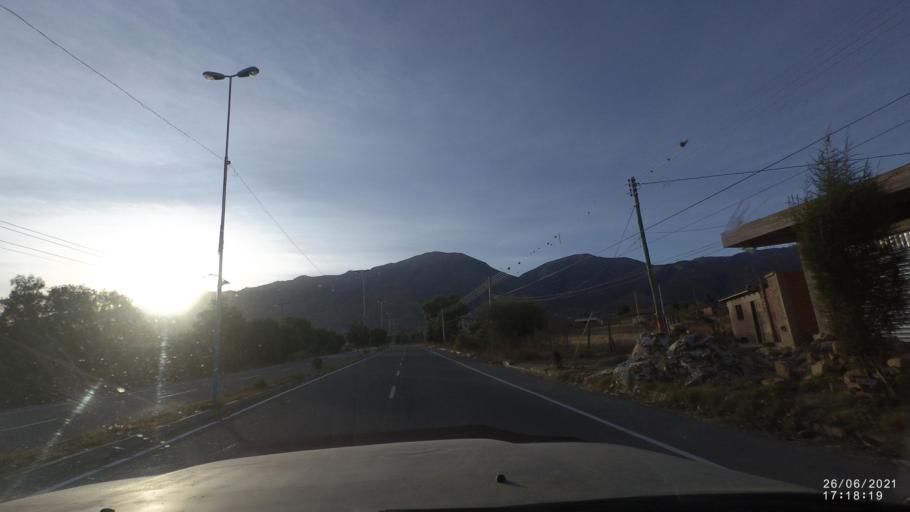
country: BO
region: Cochabamba
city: Cliza
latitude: -17.5373
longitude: -65.9607
